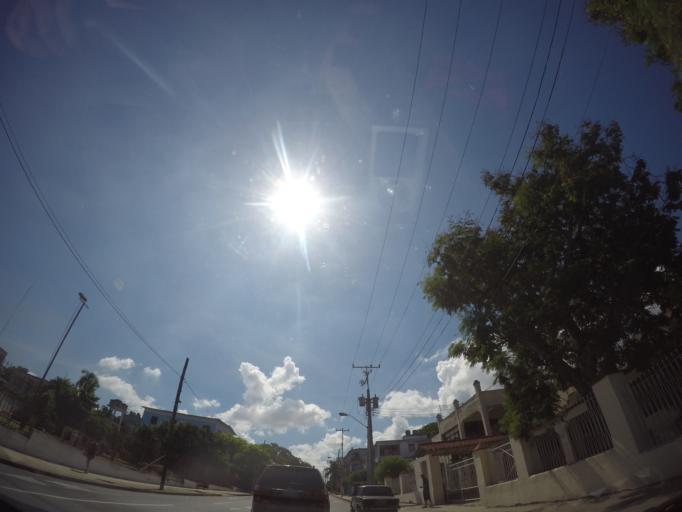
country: CU
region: La Habana
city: Regla
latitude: 23.0965
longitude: -82.3171
